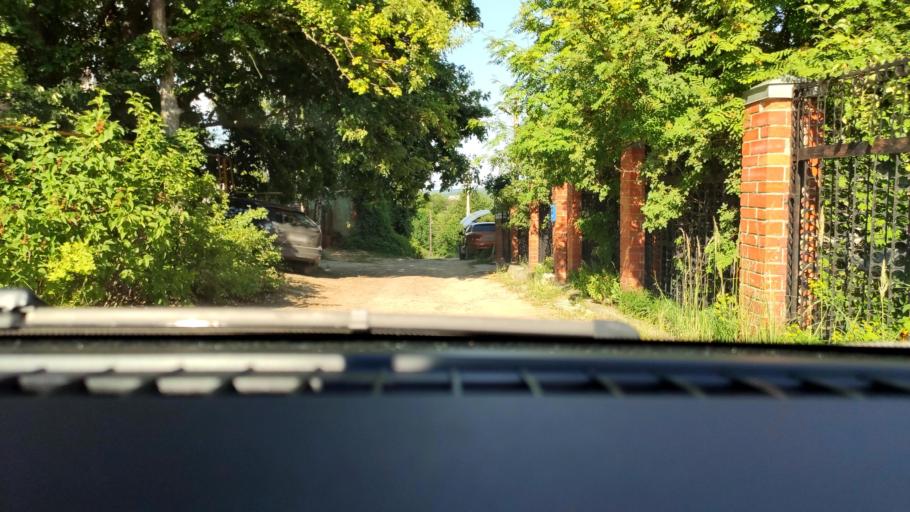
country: RU
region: Voronezj
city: Ramon'
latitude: 51.8153
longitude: 39.2685
